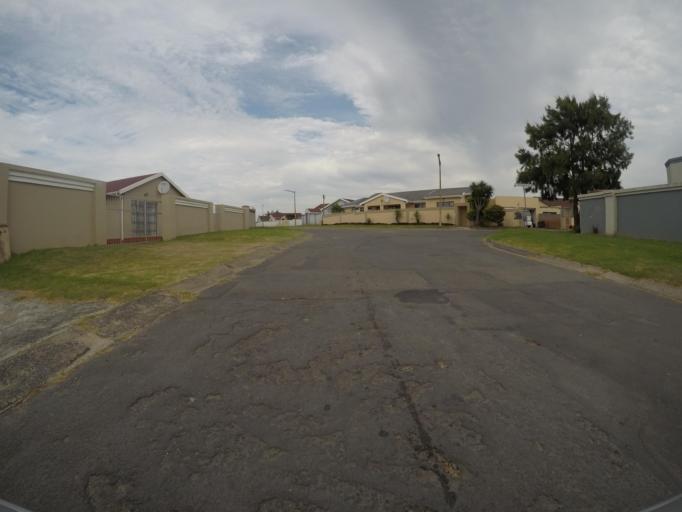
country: ZA
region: Eastern Cape
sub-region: Buffalo City Metropolitan Municipality
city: East London
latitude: -32.9774
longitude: 27.8614
